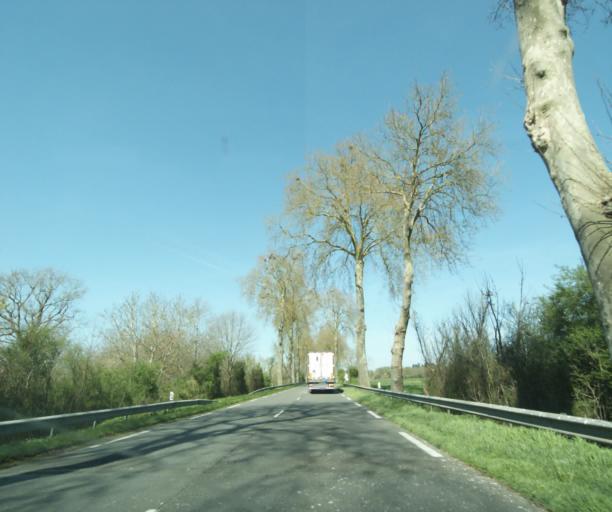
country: FR
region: Bourgogne
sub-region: Departement de la Nievre
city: Chantenay-Saint-Imbert
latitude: 46.7208
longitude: 3.1819
